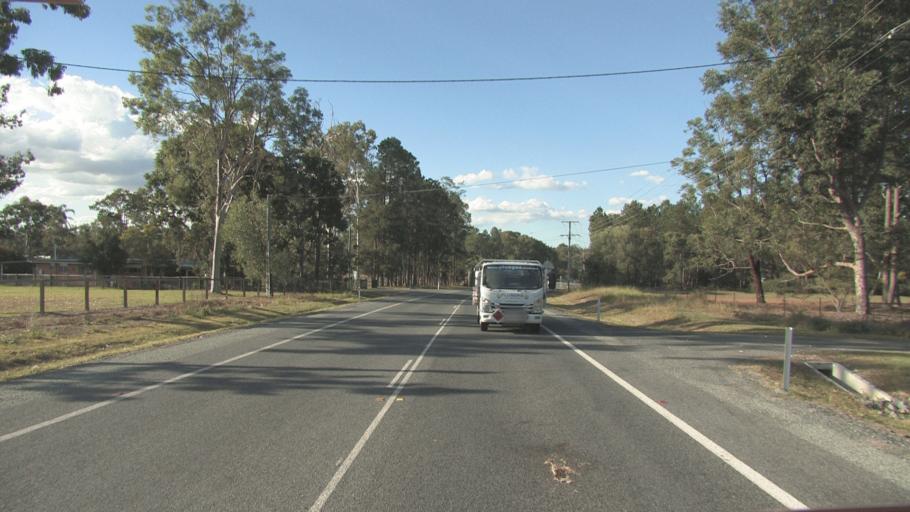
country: AU
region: Queensland
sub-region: Logan
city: Park Ridge South
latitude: -27.7193
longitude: 152.9687
